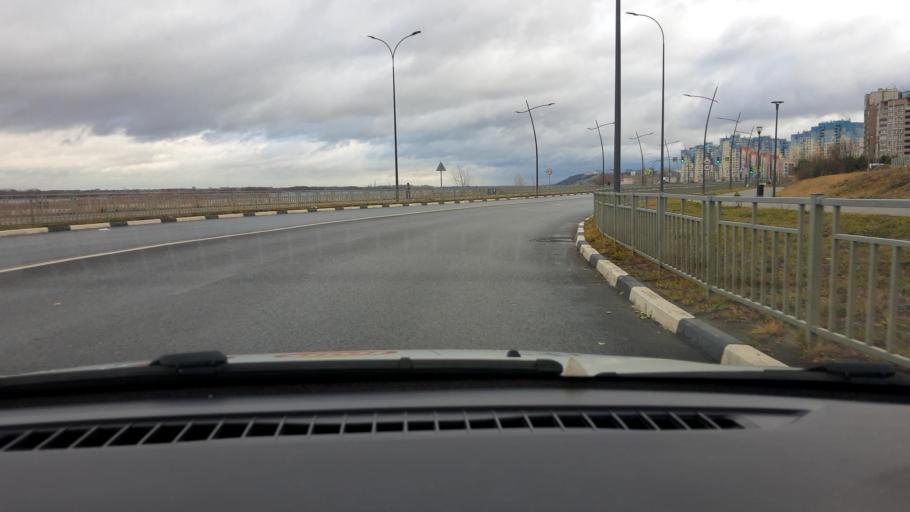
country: RU
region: Nizjnij Novgorod
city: Nizhniy Novgorod
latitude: 56.3475
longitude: 43.9375
